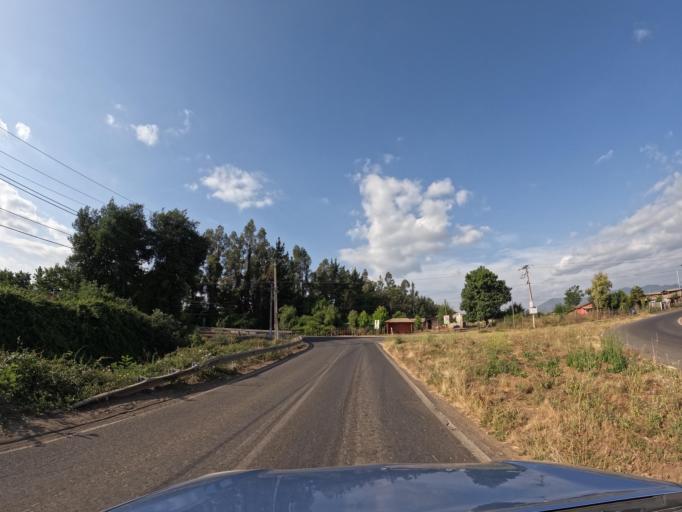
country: CL
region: Maule
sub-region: Provincia de Curico
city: Molina
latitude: -35.2611
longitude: -71.2442
